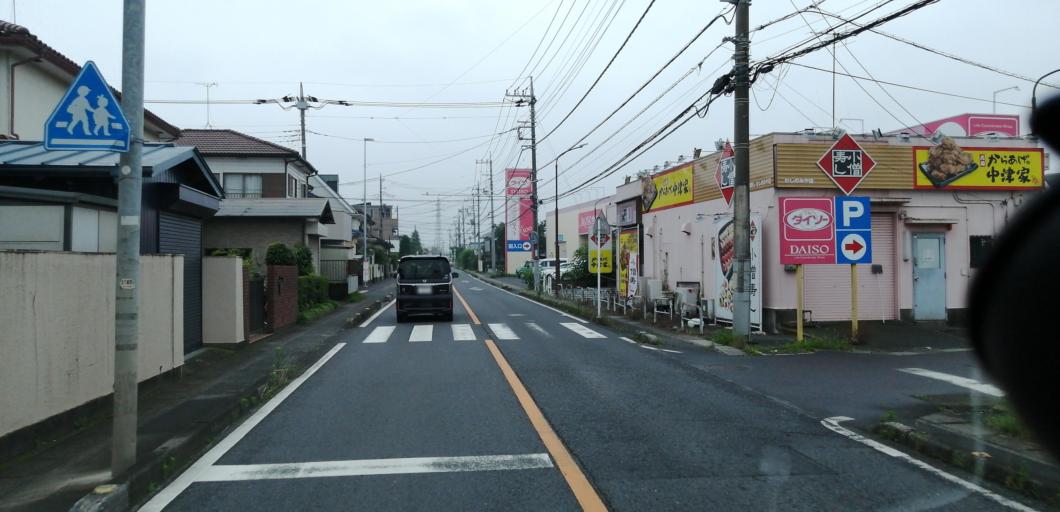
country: JP
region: Saitama
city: Kukichuo
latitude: 36.0989
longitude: 139.6721
